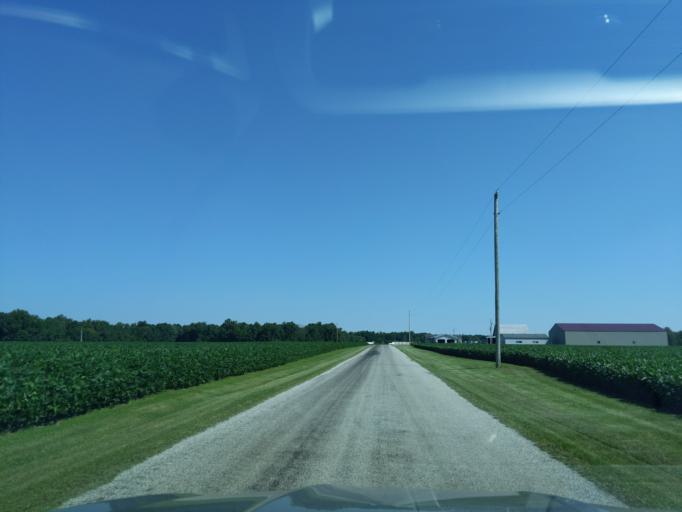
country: US
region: Indiana
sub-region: Ripley County
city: Osgood
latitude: 39.0862
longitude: -85.4330
